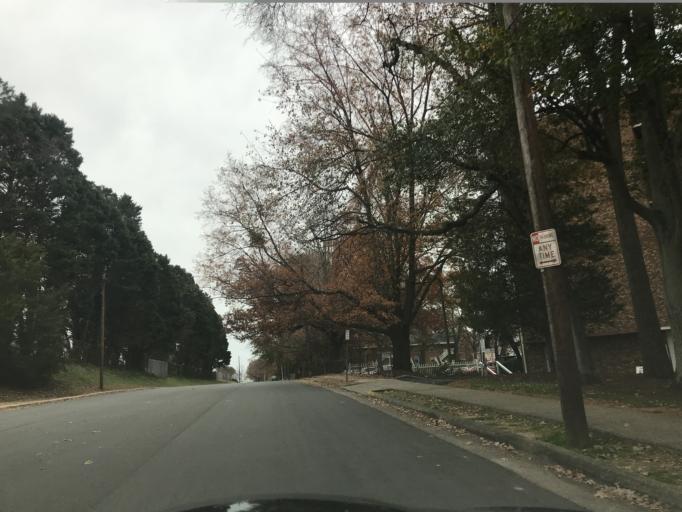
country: US
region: North Carolina
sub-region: Wake County
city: West Raleigh
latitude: 35.7910
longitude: -78.6568
